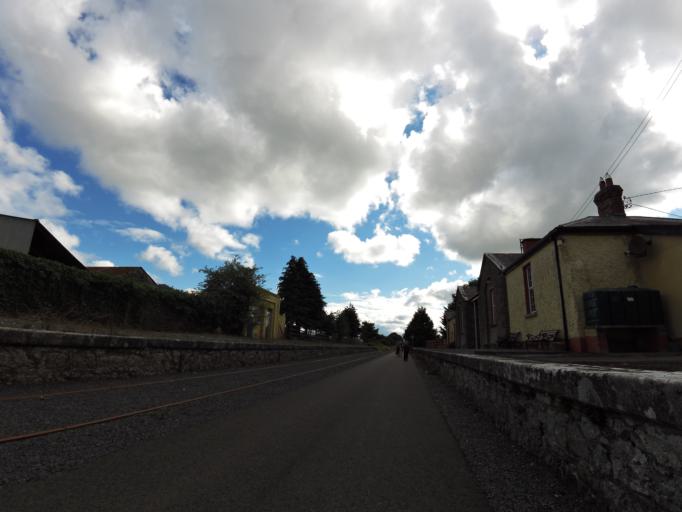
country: IE
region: Leinster
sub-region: An Iarmhi
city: Kilbeggan
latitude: 53.4633
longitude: -7.5061
